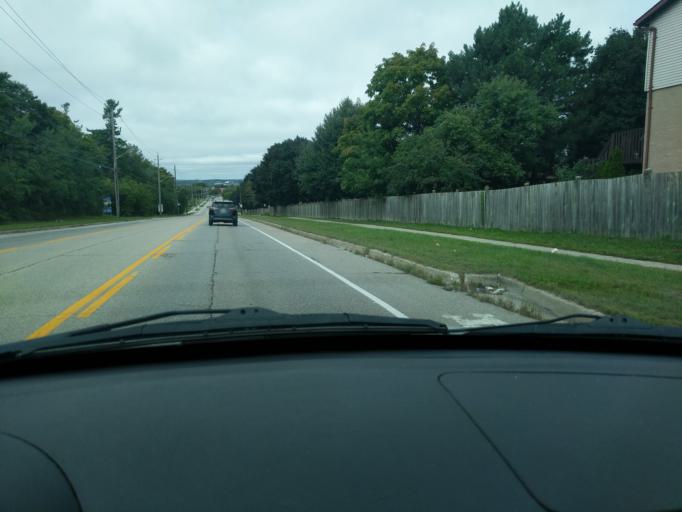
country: CA
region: Ontario
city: Cambridge
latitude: 43.4179
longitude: -80.3123
